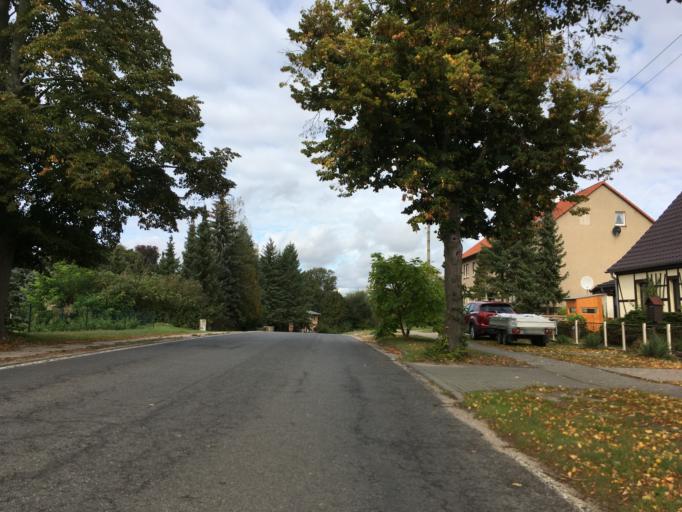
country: DE
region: Brandenburg
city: Oderberg
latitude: 52.9150
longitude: 14.1165
